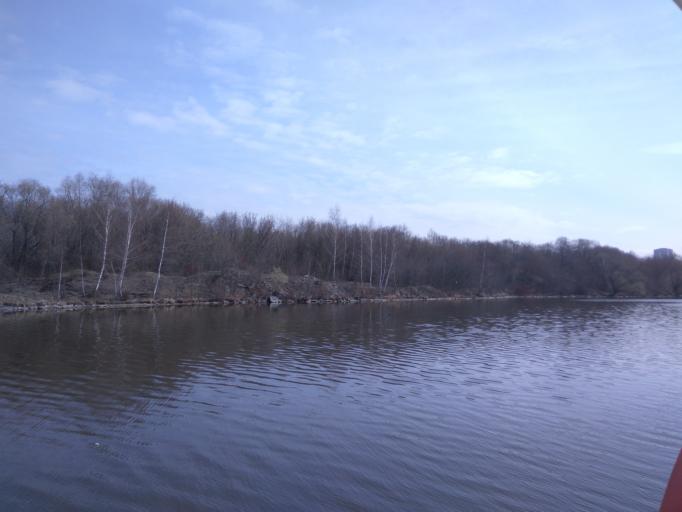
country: RU
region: Moscow
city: Kolomenskoye
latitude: 55.6910
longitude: 37.7005
